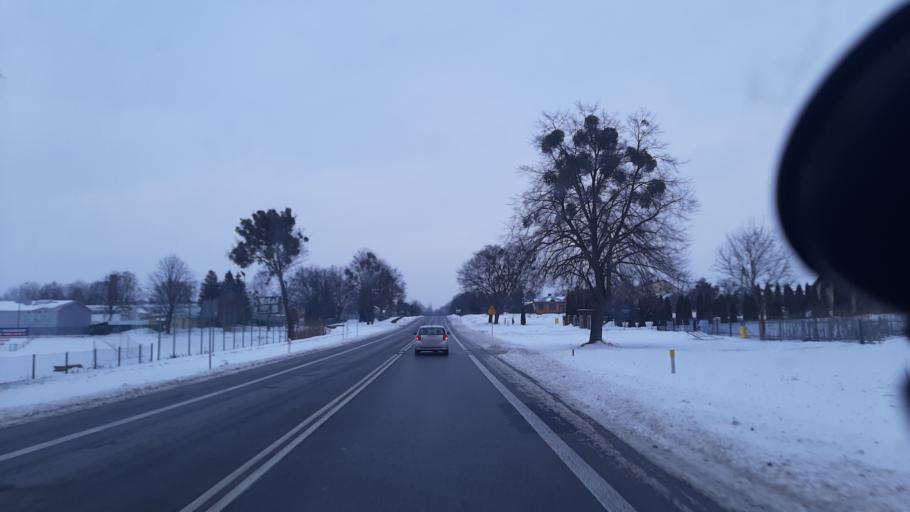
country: PL
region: Lublin Voivodeship
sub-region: Powiat lubelski
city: Garbow
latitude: 51.3587
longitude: 22.3171
